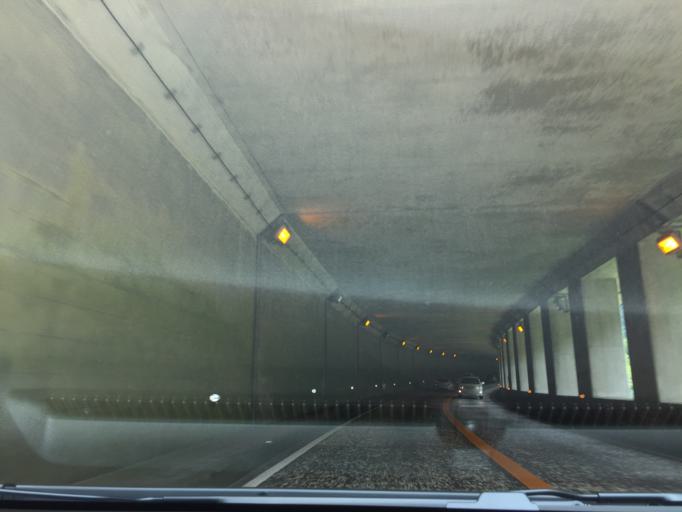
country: JP
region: Gifu
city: Gujo
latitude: 35.7720
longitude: 137.2258
